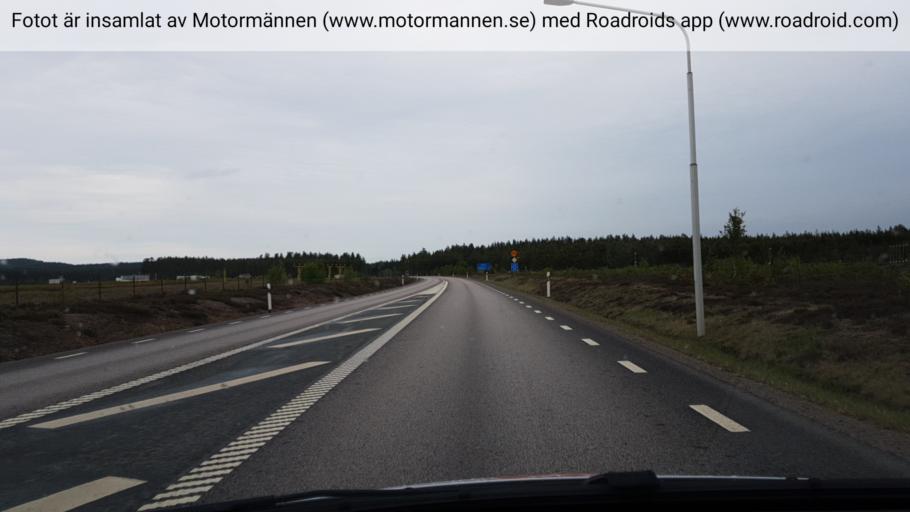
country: SE
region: Kalmar
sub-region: Hultsfreds Kommun
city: Hultsfred
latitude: 57.5186
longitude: 15.8429
